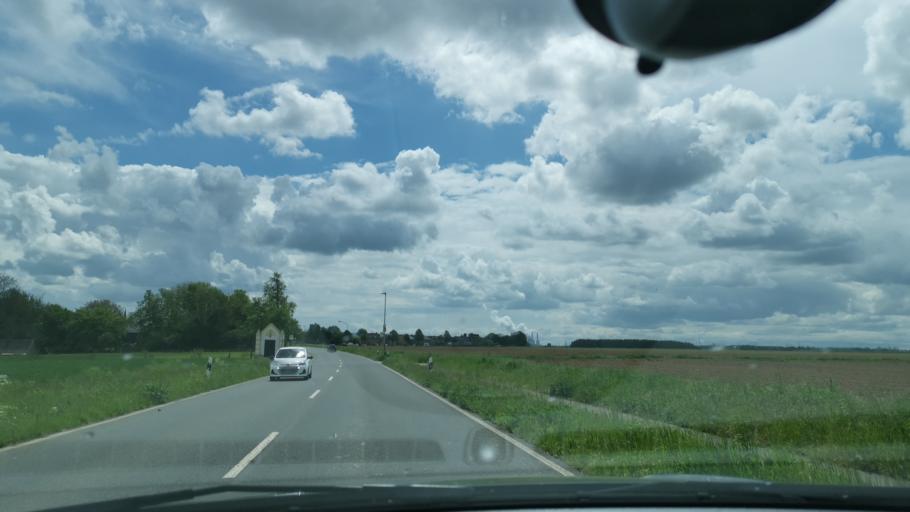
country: DE
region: North Rhine-Westphalia
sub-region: Regierungsbezirk Dusseldorf
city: Rommerskirchen
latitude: 51.0794
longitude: 6.6879
